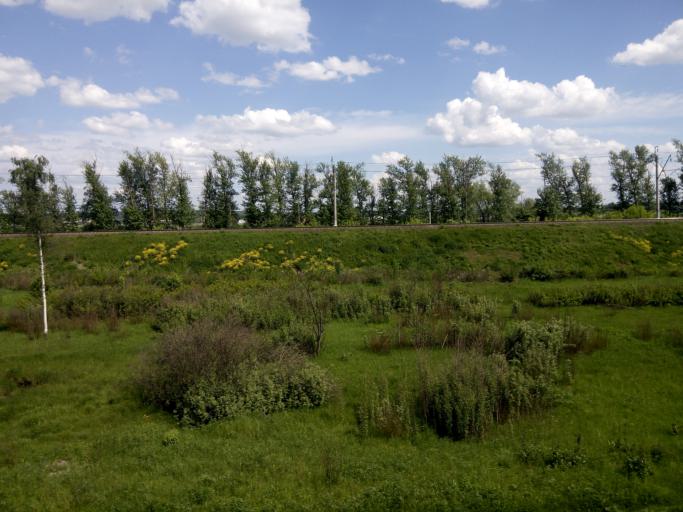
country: RU
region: Moskovskaya
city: Yam
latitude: 55.4923
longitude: 37.7285
